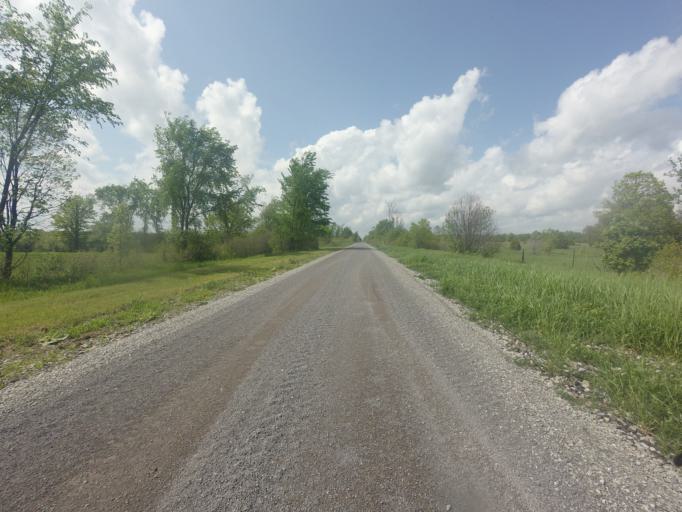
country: CA
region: Ontario
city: Carleton Place
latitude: 45.0294
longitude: -76.0793
